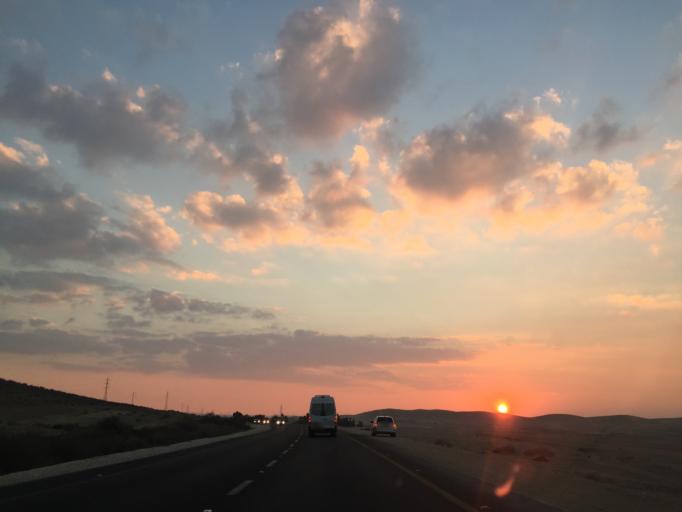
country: IL
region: Southern District
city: Yeroham
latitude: 31.0352
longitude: 34.8042
